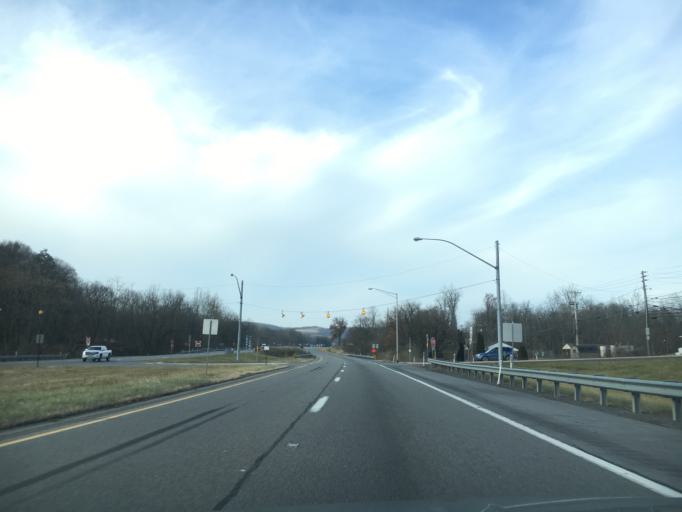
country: US
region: Pennsylvania
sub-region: Montour County
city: Danville
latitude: 40.9820
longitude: -76.6271
